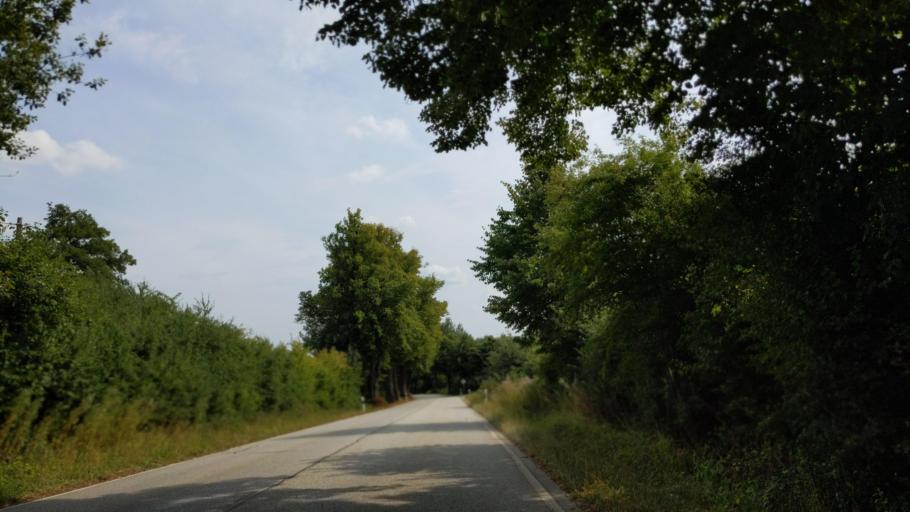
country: DE
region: Mecklenburg-Vorpommern
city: Selmsdorf
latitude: 53.8563
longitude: 10.9177
